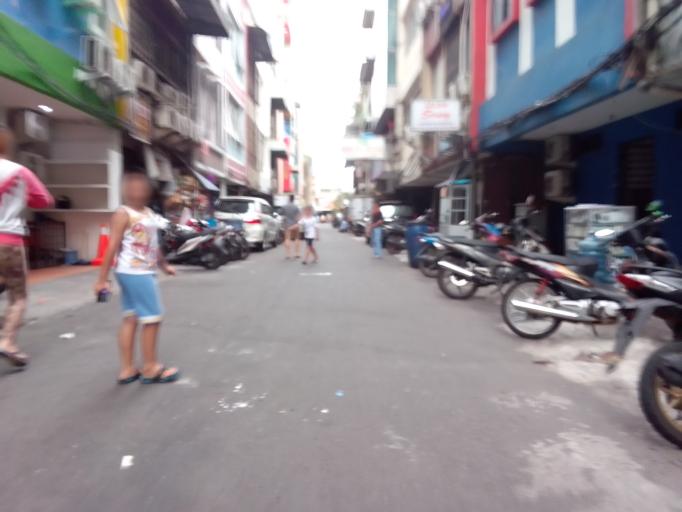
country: ID
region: Jakarta Raya
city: Jakarta
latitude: -6.1502
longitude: 106.8214
